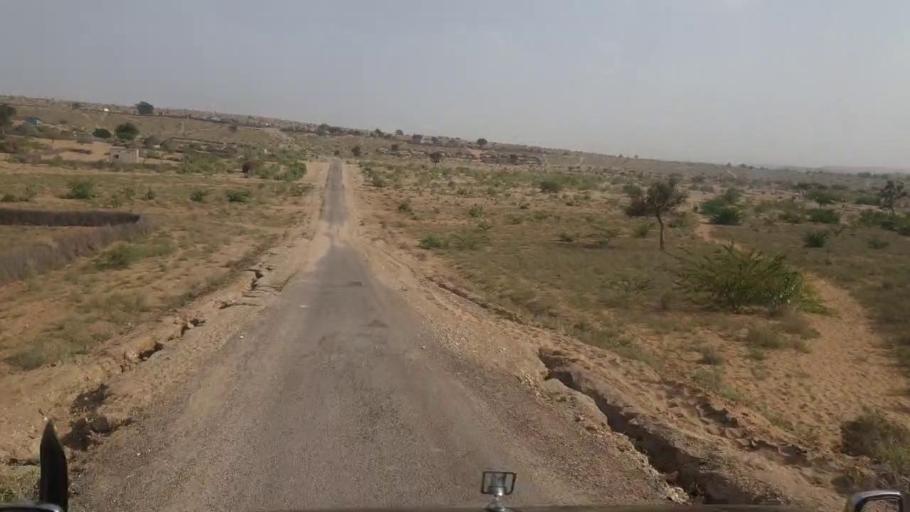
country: PK
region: Sindh
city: Islamkot
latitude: 25.1378
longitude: 70.3197
